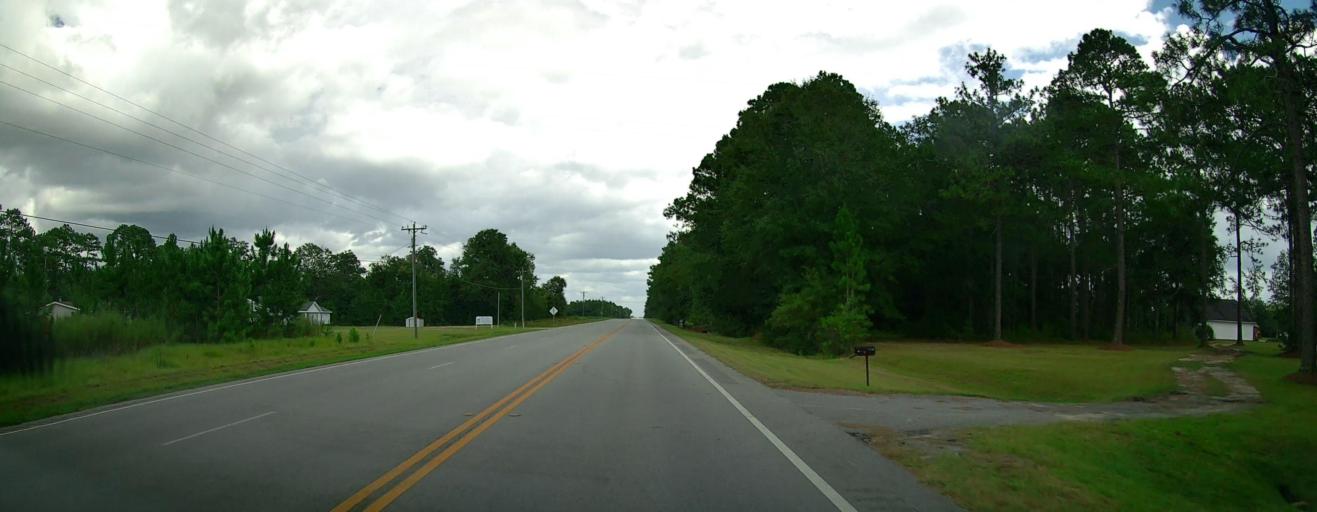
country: US
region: Georgia
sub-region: Coffee County
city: Broxton
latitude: 31.5706
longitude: -83.0229
